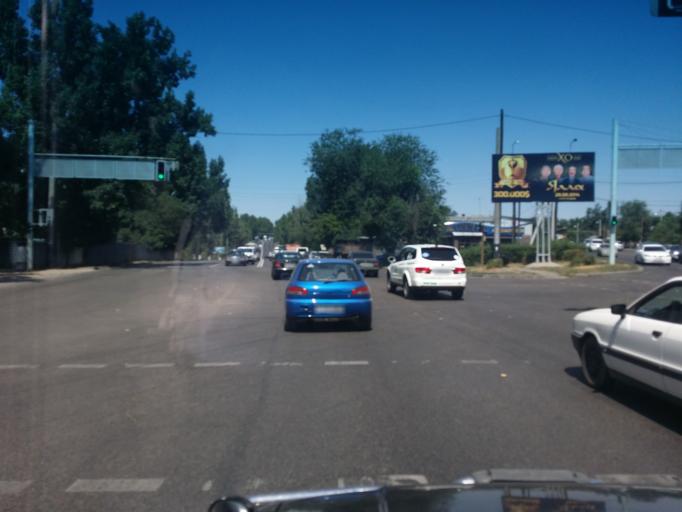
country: KZ
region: Almaty Oblysy
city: Pervomayskiy
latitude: 43.3318
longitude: 76.9330
